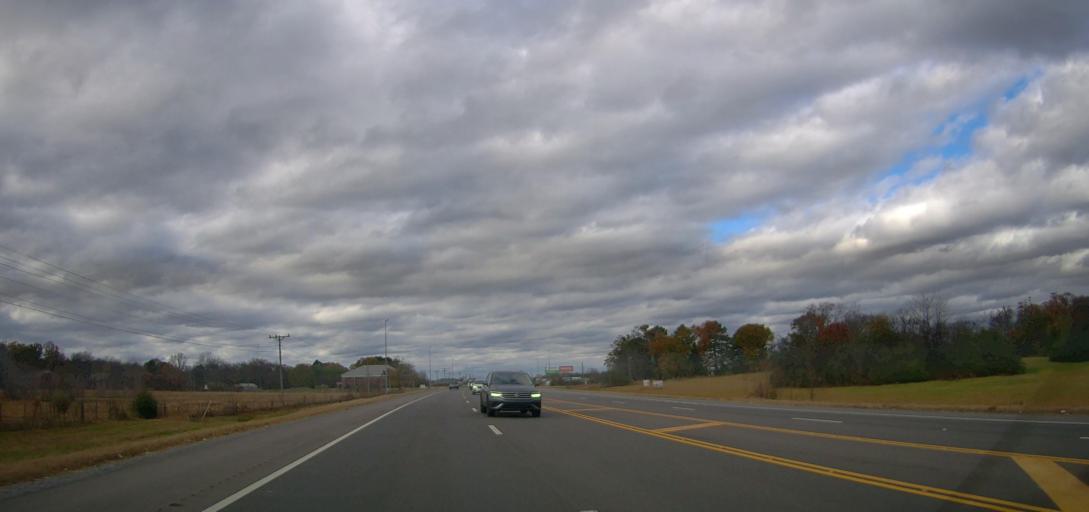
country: US
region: Alabama
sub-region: Lawrence County
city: Moulton
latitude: 34.4720
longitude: -87.2674
